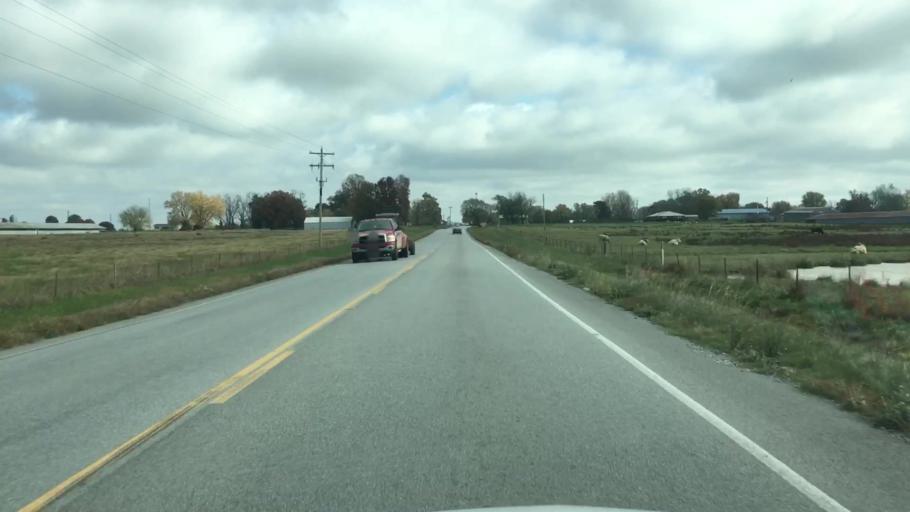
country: US
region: Arkansas
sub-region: Benton County
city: Gentry
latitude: 36.2617
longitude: -94.3635
